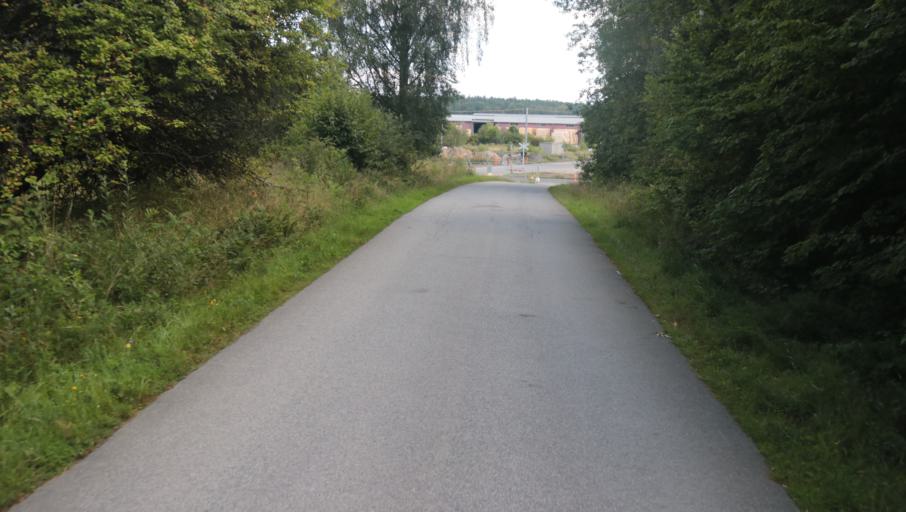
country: SE
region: Blekinge
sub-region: Karlshamns Kommun
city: Karlshamn
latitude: 56.1640
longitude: 14.8166
